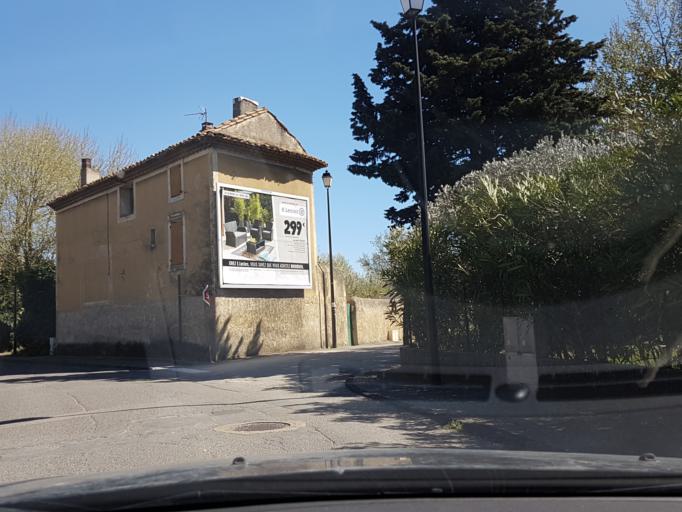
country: FR
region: Provence-Alpes-Cote d'Azur
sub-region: Departement du Vaucluse
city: Sarrians
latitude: 44.0803
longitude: 4.9714
